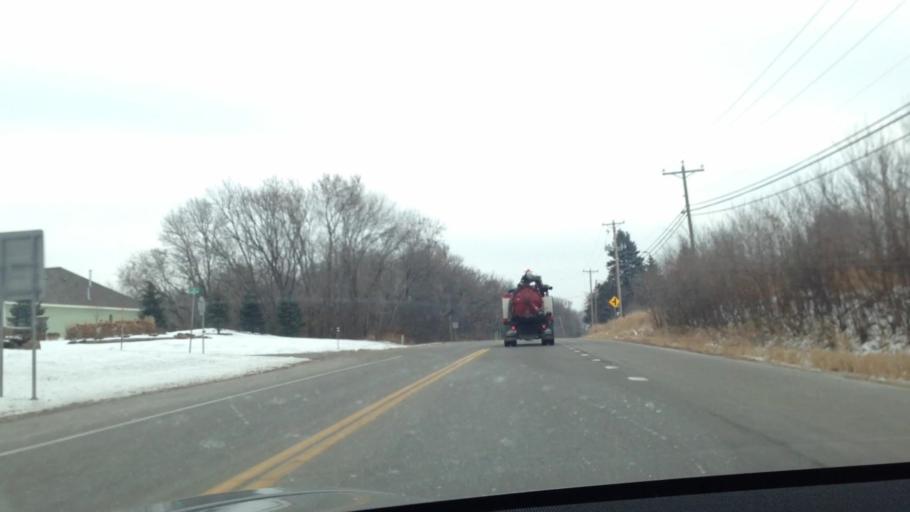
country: US
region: Minnesota
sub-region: Washington County
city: Forest Lake
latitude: 45.2538
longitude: -92.9957
